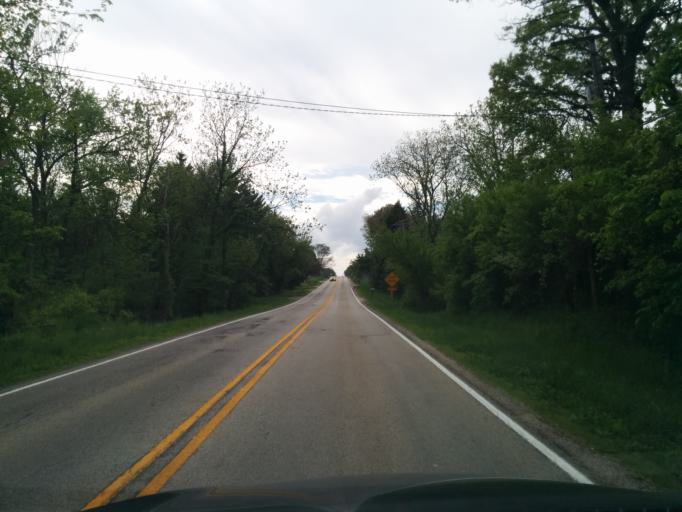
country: US
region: Illinois
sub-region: Cook County
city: Lemont
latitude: 41.6416
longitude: -88.0238
